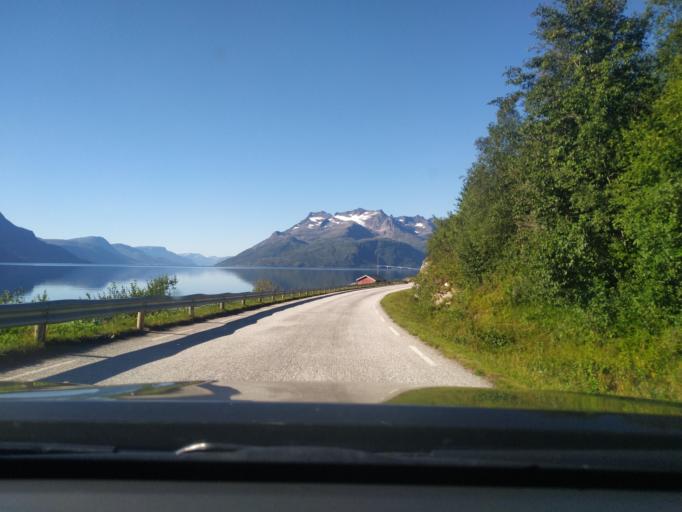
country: NO
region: Troms
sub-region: Dyroy
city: Brostadbotn
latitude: 68.9220
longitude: 17.6267
